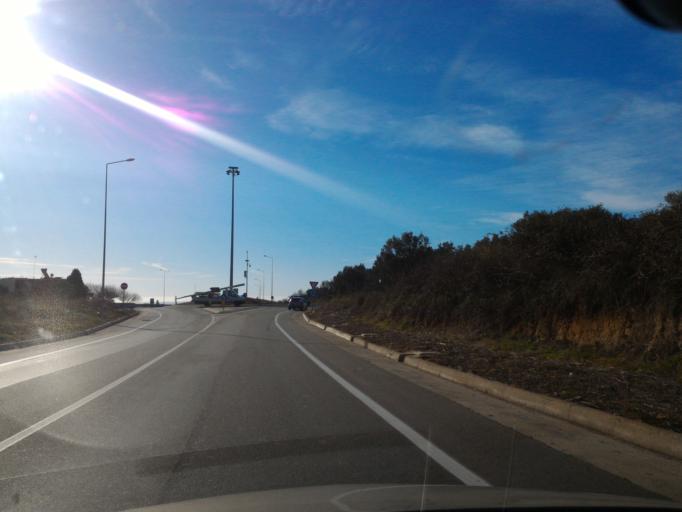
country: IT
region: Calabria
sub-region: Provincia di Crotone
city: Isola di Capo Rizzuto
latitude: 38.9514
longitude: 17.0826
